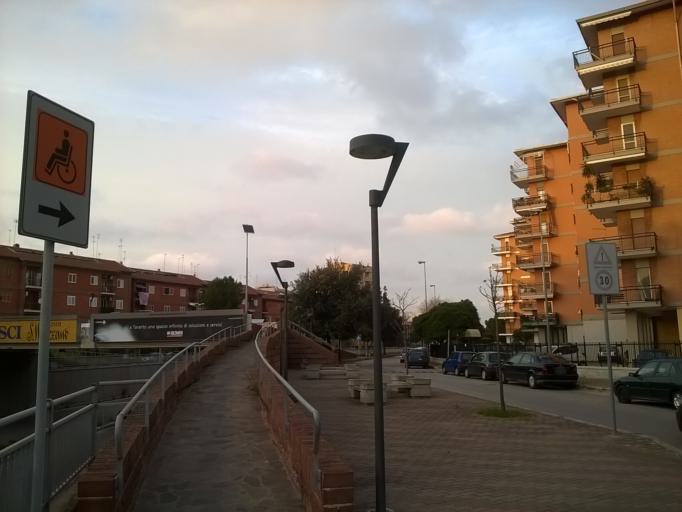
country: IT
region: Apulia
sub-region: Provincia di Taranto
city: Taranto
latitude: 40.4475
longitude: 17.2597
